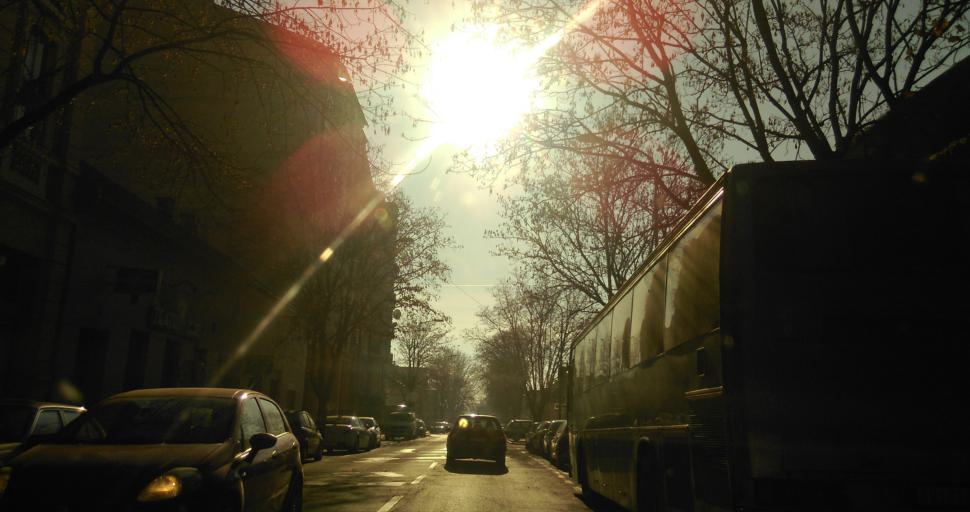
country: RS
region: Autonomna Pokrajina Vojvodina
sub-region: Sremski Okrug
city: Ruma
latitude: 45.0065
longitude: 19.8225
